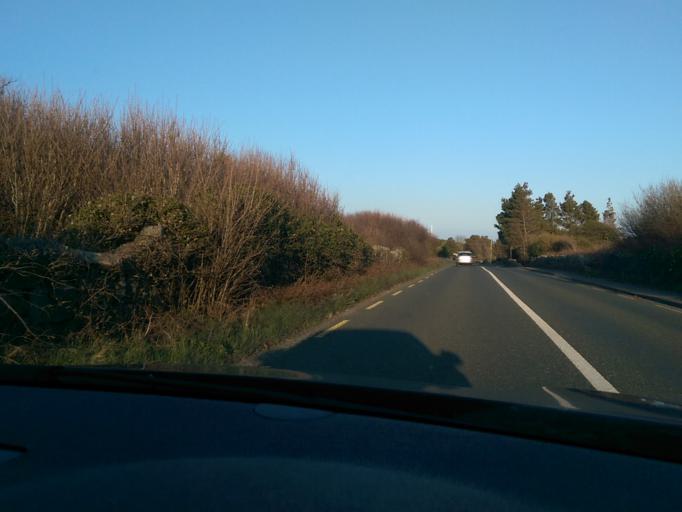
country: IE
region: Connaught
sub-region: County Galway
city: Bearna
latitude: 53.2464
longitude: -9.2644
